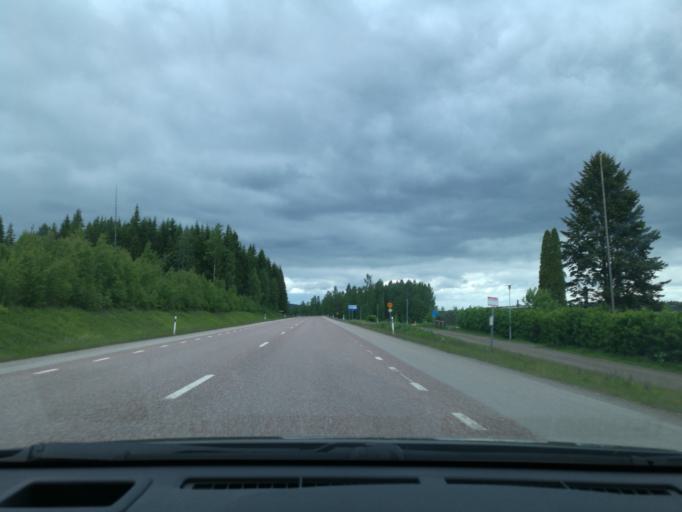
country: SE
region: Dalarna
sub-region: Smedjebackens Kommun
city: Smedjebacken
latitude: 60.1208
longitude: 15.4743
